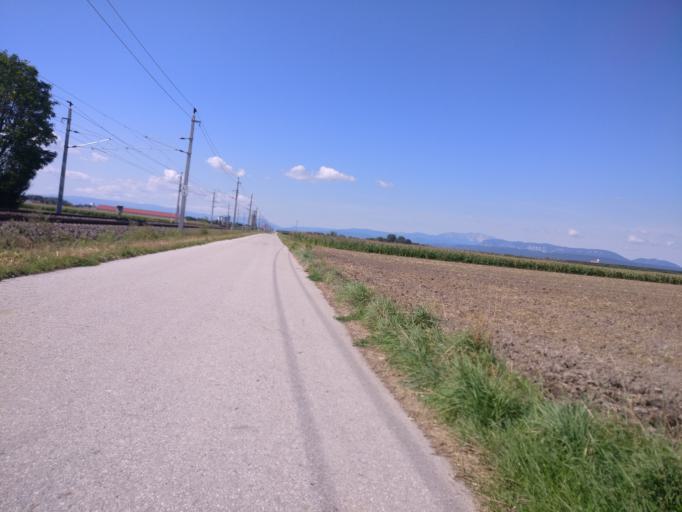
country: AT
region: Lower Austria
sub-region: Politischer Bezirk Wiener Neustadt
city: Zillingdorf
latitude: 47.8579
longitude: 16.3137
